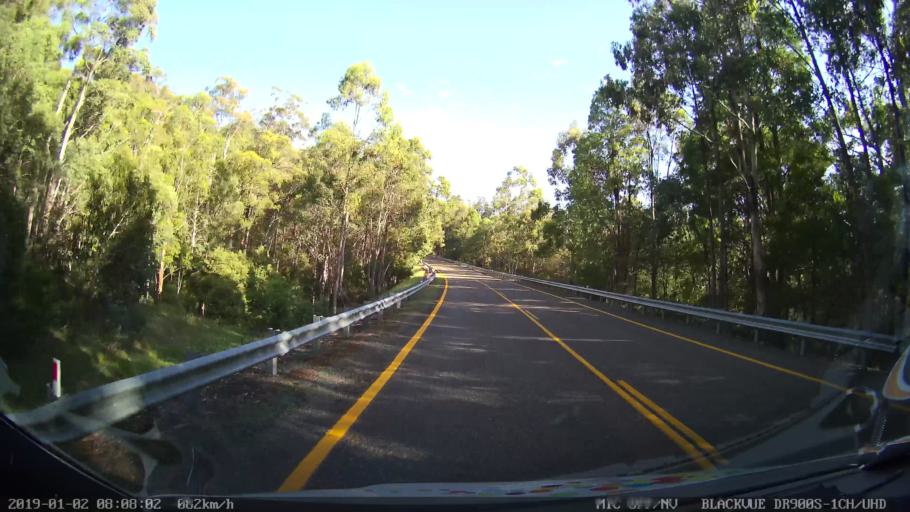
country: AU
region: New South Wales
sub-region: Tumut Shire
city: Tumut
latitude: -35.6202
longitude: 148.3885
